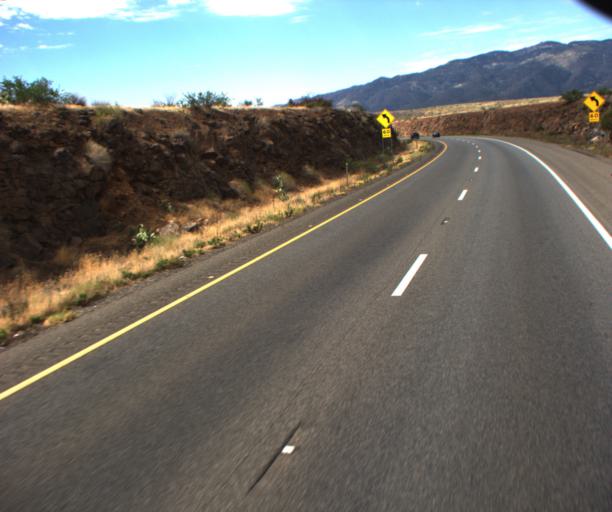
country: US
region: Arizona
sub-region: Yavapai County
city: Black Canyon City
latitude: 34.1716
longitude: -112.1405
